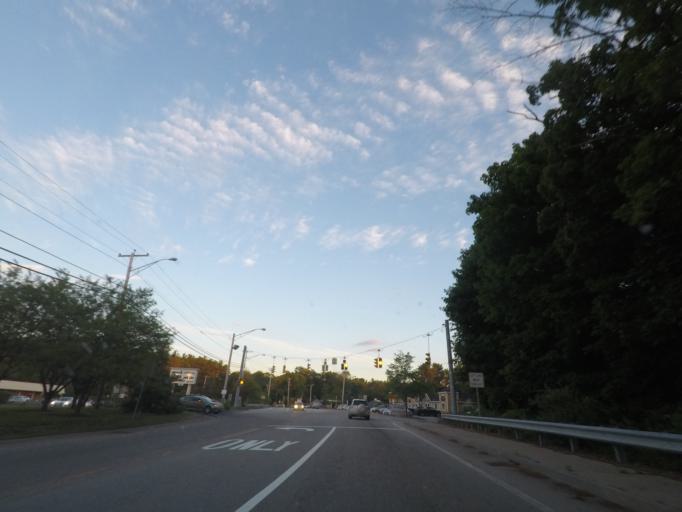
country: US
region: Massachusetts
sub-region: Worcester County
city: Sturbridge
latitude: 42.0974
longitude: -72.0727
